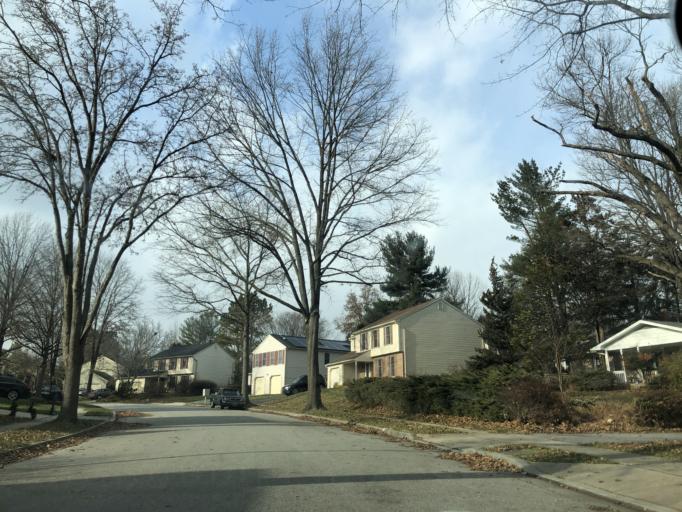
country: US
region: Maryland
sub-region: Howard County
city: Columbia
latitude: 39.1998
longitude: -76.8312
